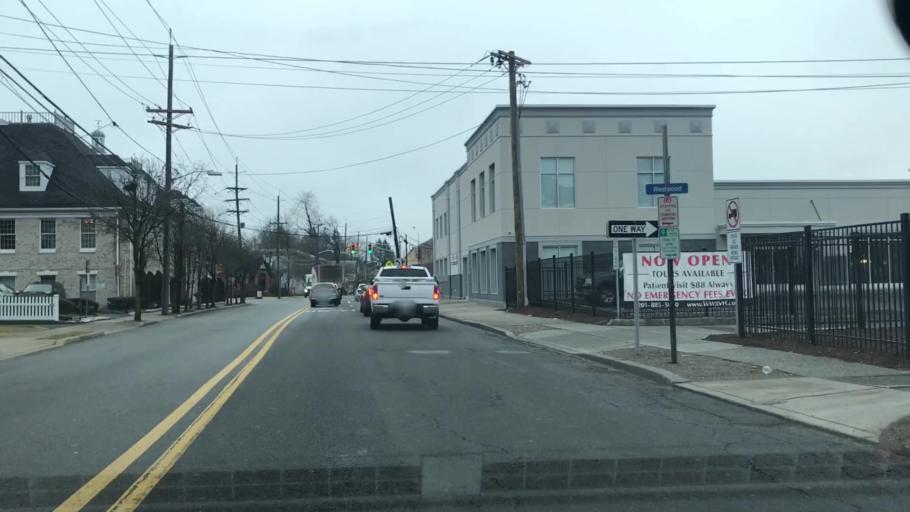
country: US
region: New Jersey
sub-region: Bergen County
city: Westwood
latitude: 40.9939
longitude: -74.0302
